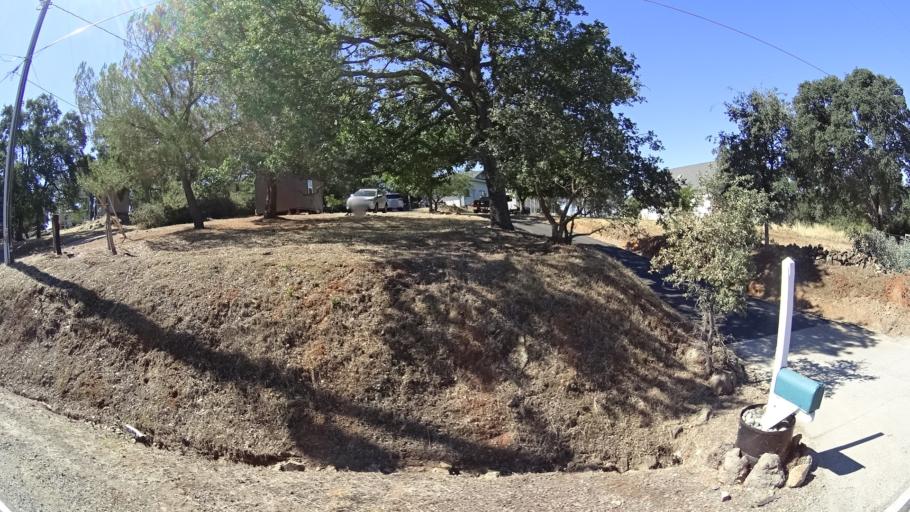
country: US
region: California
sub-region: Calaveras County
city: Rancho Calaveras
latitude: 38.1083
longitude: -120.8633
